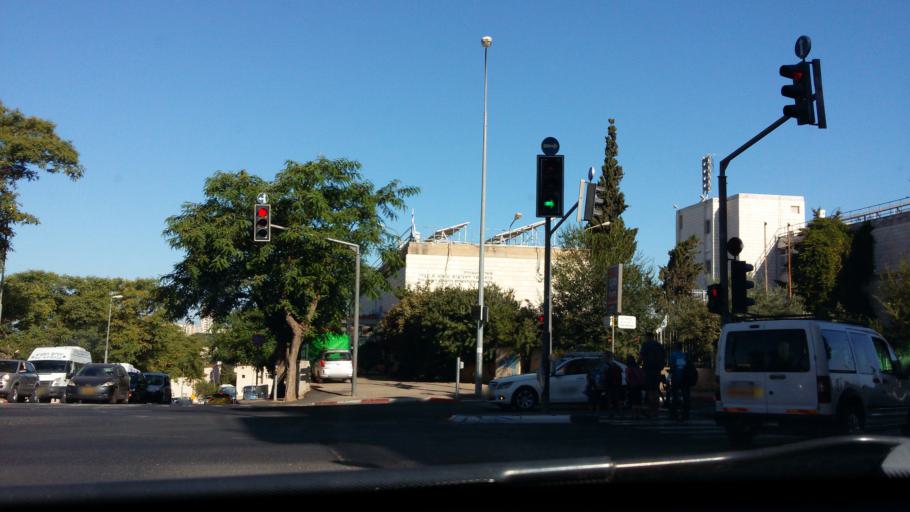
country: IL
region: Jerusalem
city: Jerusalem
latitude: 31.7552
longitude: 35.2147
